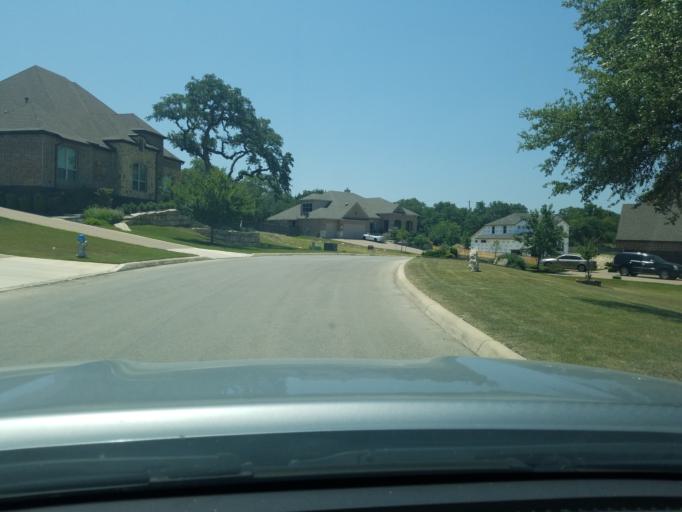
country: US
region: Texas
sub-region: Bexar County
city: Timberwood Park
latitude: 29.7107
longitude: -98.5032
